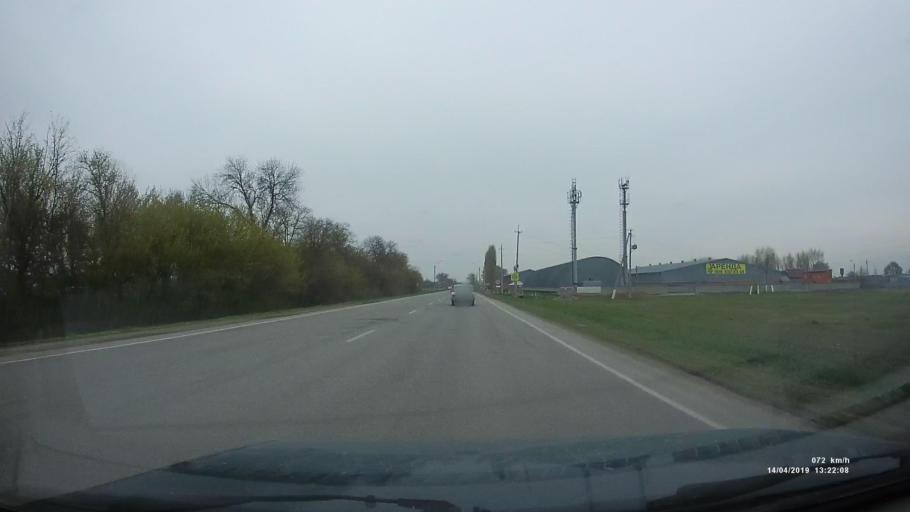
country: RU
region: Rostov
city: Kuleshovka
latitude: 47.0824
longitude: 39.5140
